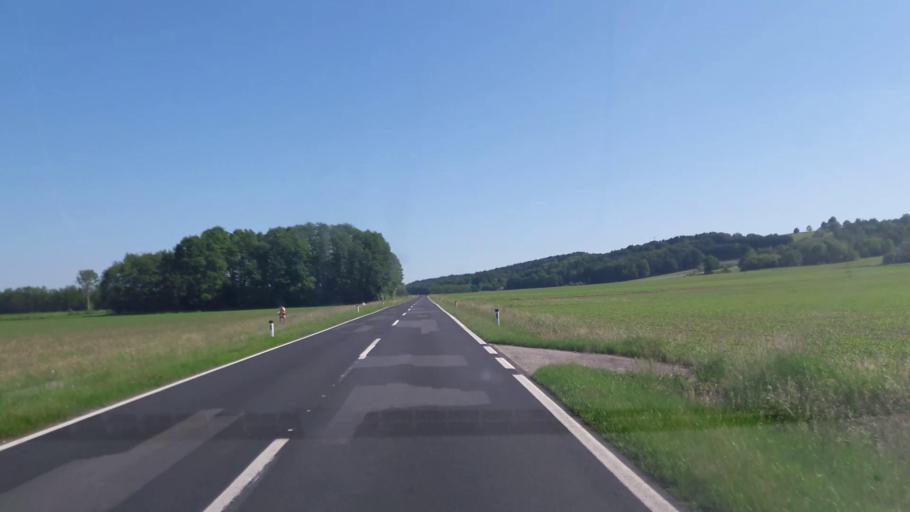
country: AT
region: Burgenland
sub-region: Politischer Bezirk Jennersdorf
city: Deutsch Kaltenbrunn
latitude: 47.0981
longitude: 16.1075
